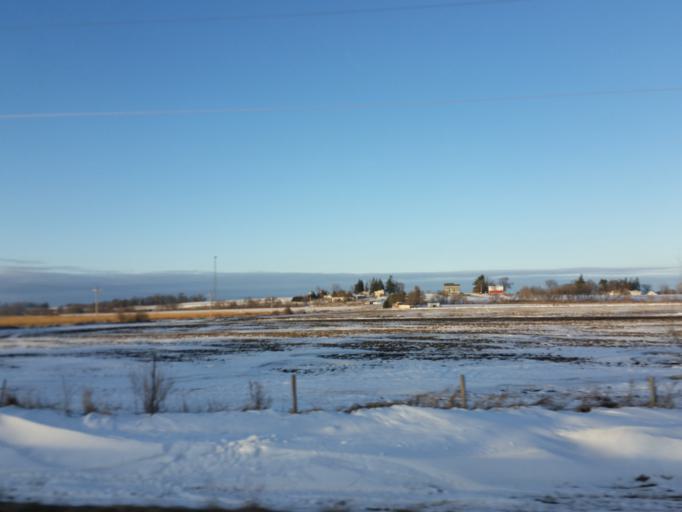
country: US
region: Iowa
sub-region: Butler County
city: Aplington
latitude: 42.7450
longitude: -92.9848
